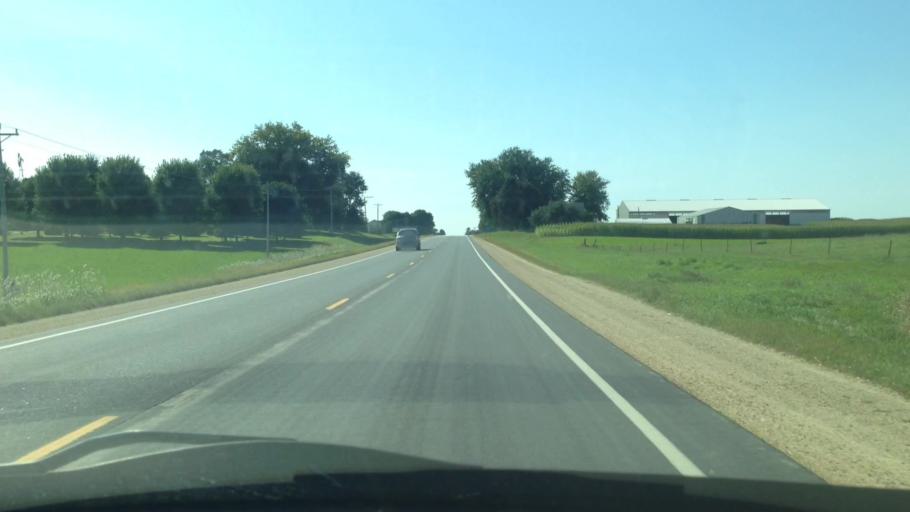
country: US
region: Minnesota
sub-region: Winona County
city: Lewiston
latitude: 43.9697
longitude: -91.8320
